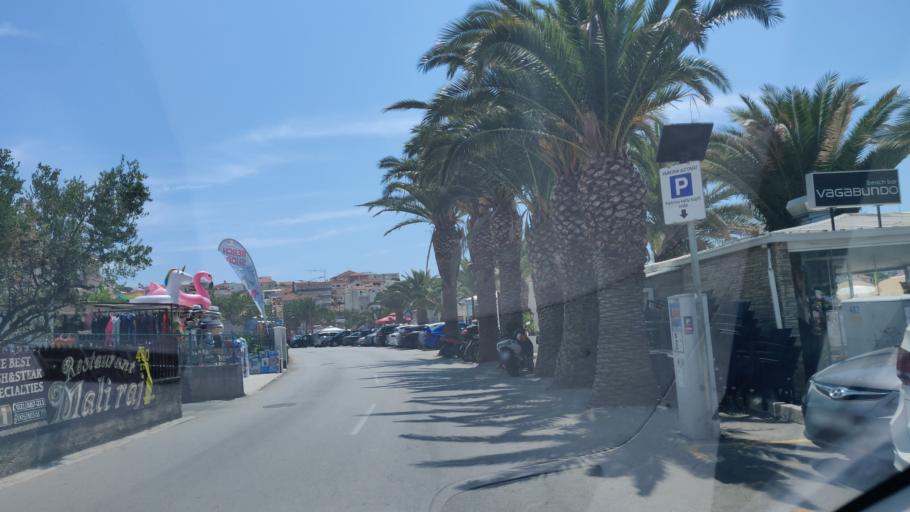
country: HR
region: Splitsko-Dalmatinska
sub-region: Grad Trogir
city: Trogir
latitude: 43.4973
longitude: 16.2605
